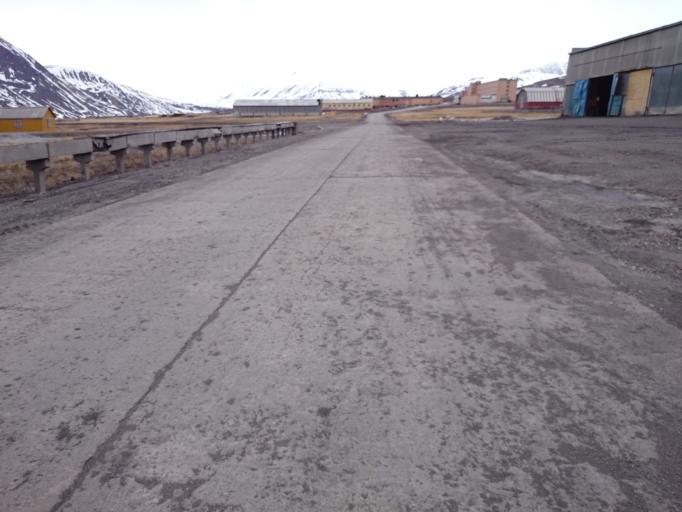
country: SJ
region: Svalbard
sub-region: Spitsbergen
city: Longyearbyen
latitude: 78.6536
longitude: 16.3402
